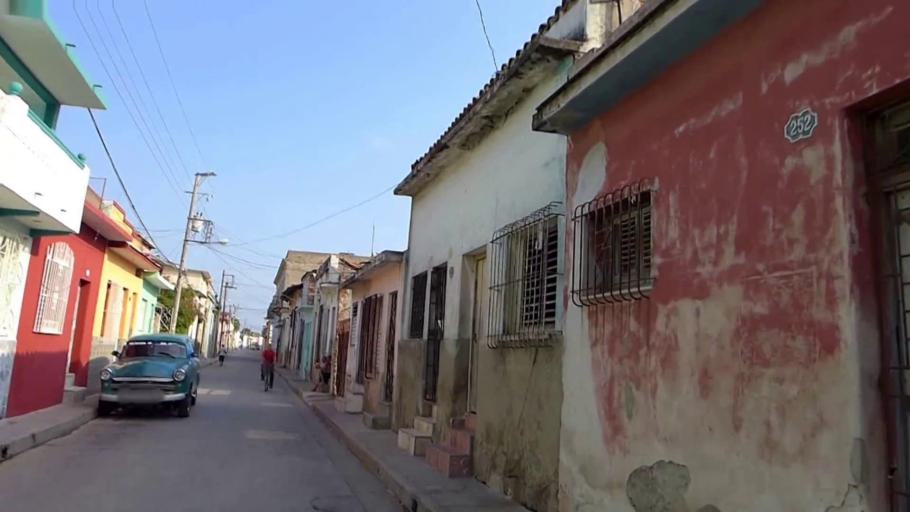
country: CU
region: Camaguey
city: Camaguey
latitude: 21.3770
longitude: -77.9210
